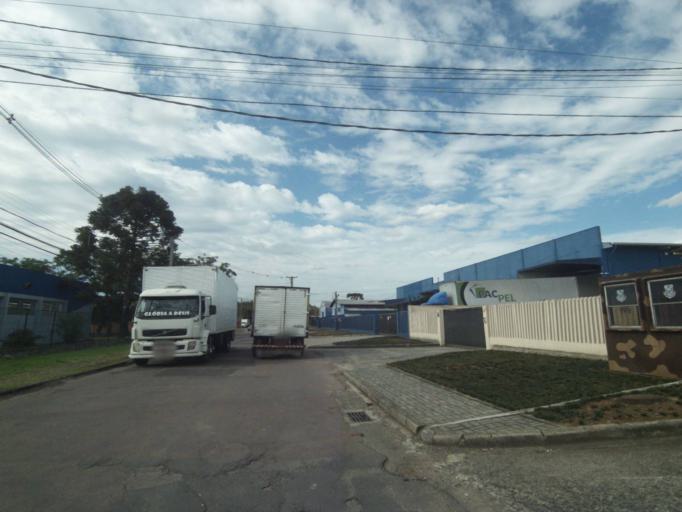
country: BR
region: Parana
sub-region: Curitiba
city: Curitiba
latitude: -25.4979
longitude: -49.3306
